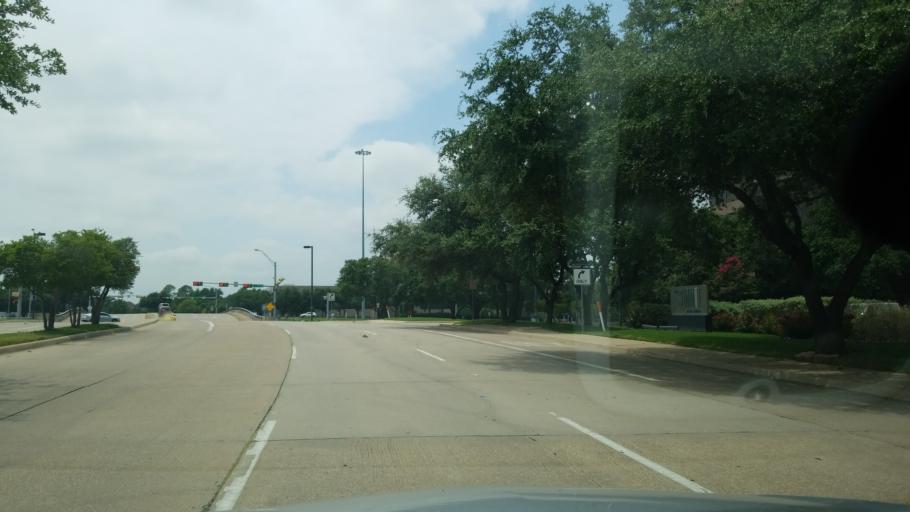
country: US
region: Texas
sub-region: Dallas County
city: Irving
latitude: 32.8592
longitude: -96.9319
